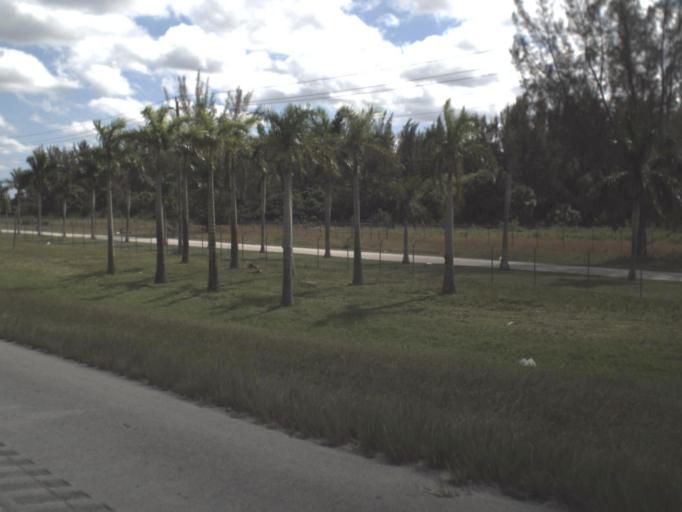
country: US
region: Florida
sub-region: Miami-Dade County
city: Lake Lucerne
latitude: 25.9714
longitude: -80.2755
